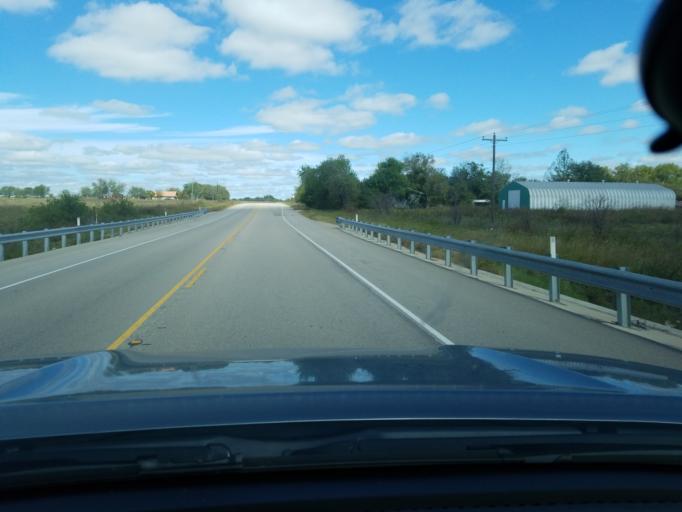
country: US
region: Texas
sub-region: Hamilton County
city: Hamilton
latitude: 31.6433
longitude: -98.1486
